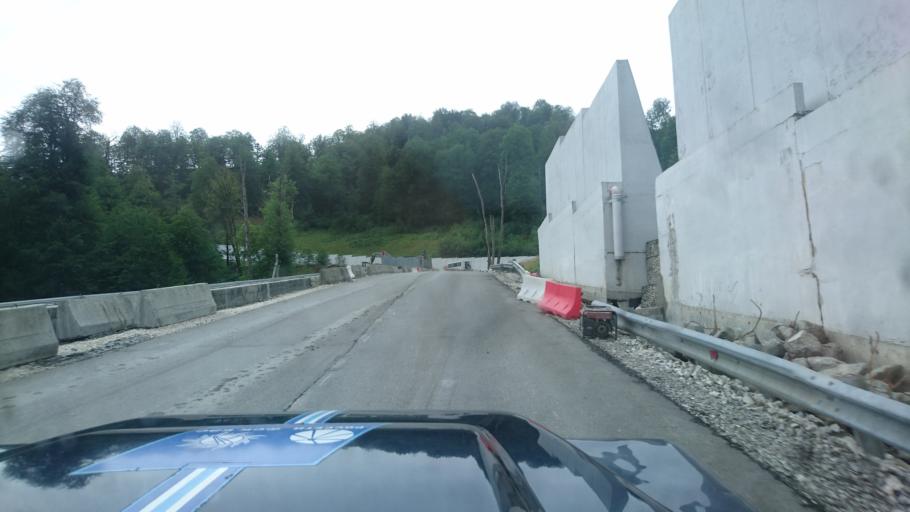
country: RU
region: Krasnodarskiy
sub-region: Sochi City
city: Krasnaya Polyana
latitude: 43.6597
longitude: 40.3094
